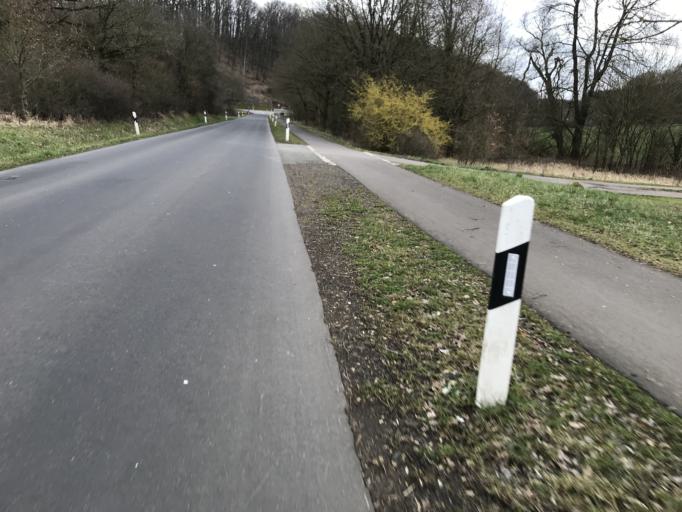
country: DE
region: Hesse
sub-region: Regierungsbezirk Giessen
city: Lich
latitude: 50.5452
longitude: 8.7914
